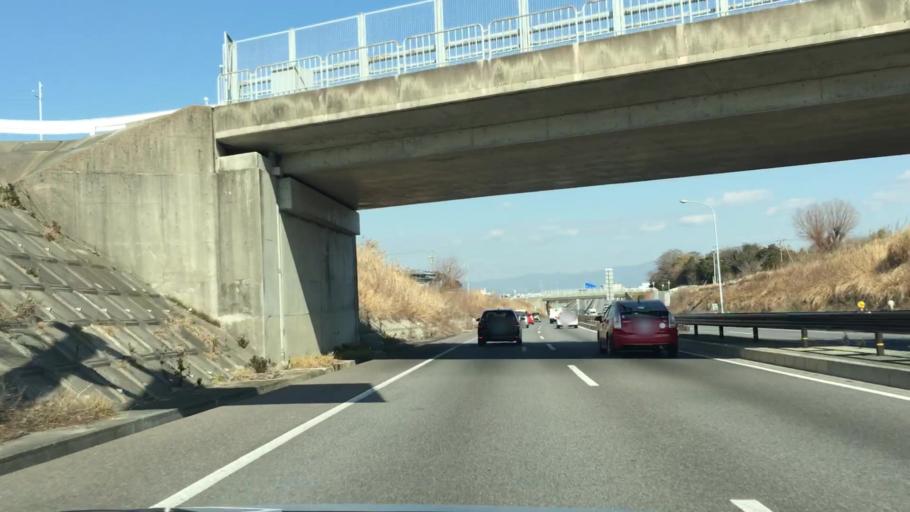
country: JP
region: Aichi
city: Toyohashi
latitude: 34.7137
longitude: 137.3520
